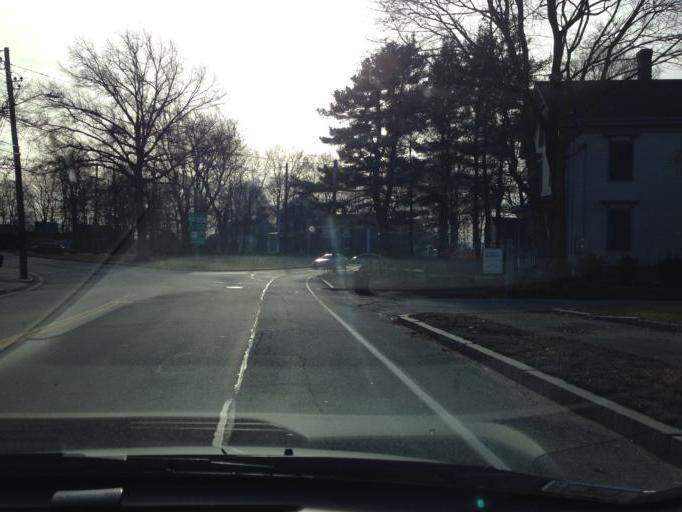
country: US
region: Massachusetts
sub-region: Middlesex County
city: Bedford
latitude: 42.4942
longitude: -71.2851
